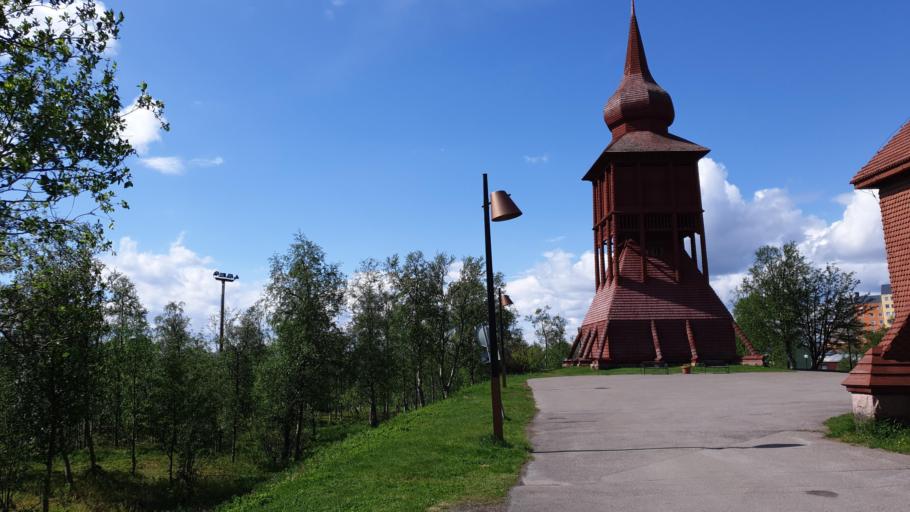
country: SE
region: Norrbotten
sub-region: Kiruna Kommun
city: Kiruna
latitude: 67.8518
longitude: 20.2329
